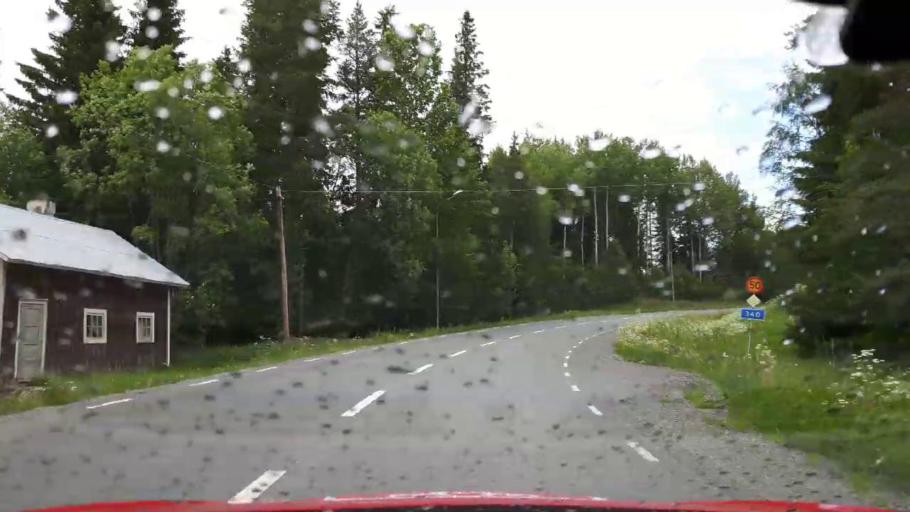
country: SE
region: Jaemtland
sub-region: Krokoms Kommun
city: Krokom
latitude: 63.5669
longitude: 14.2709
